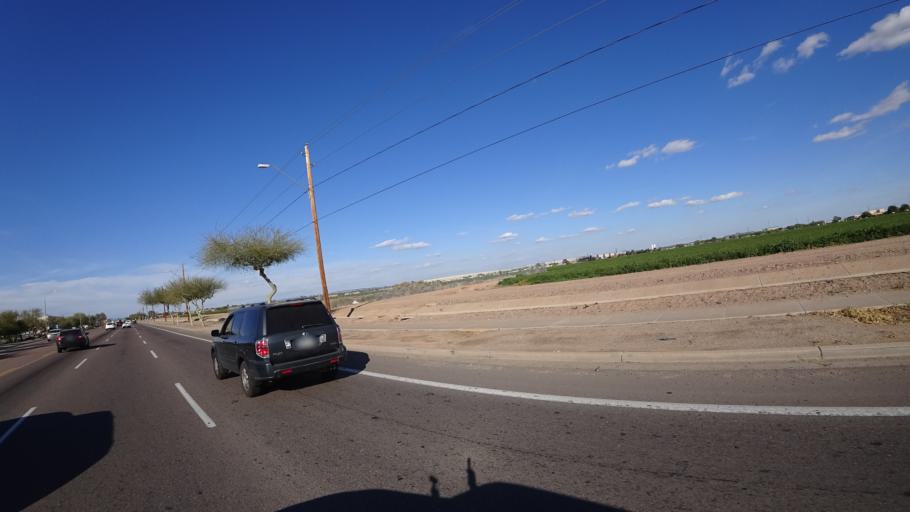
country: US
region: Arizona
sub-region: Maricopa County
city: Tolleson
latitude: 33.4532
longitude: -112.2382
